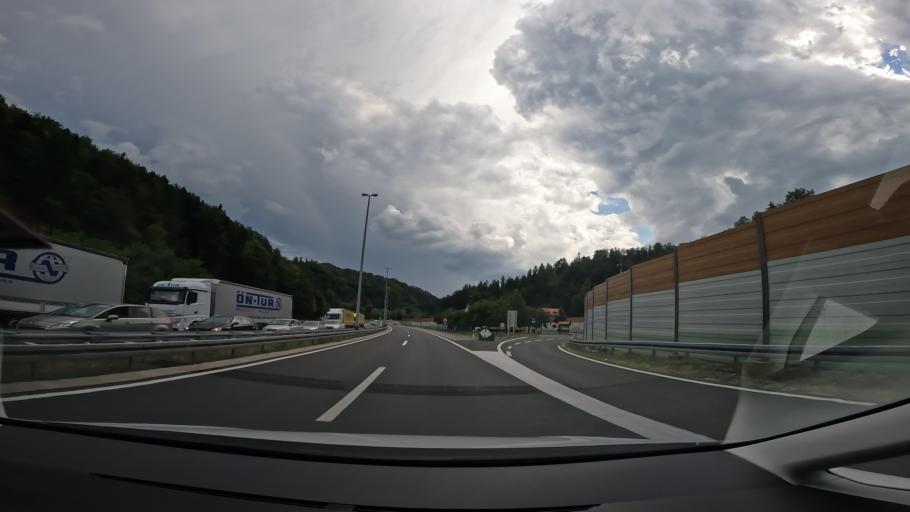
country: SI
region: Zetale
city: Zetale
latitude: 46.2420
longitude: 15.8467
